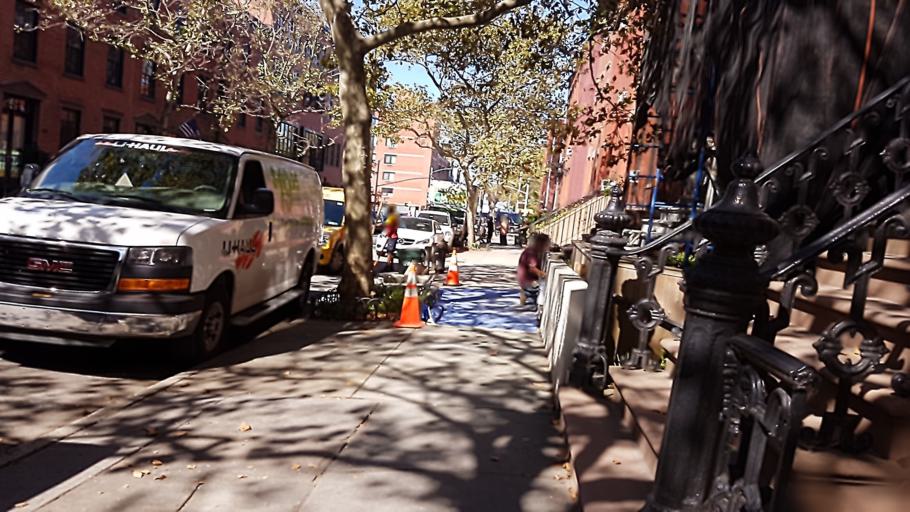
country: US
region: New York
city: New York City
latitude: 40.6891
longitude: -73.9976
